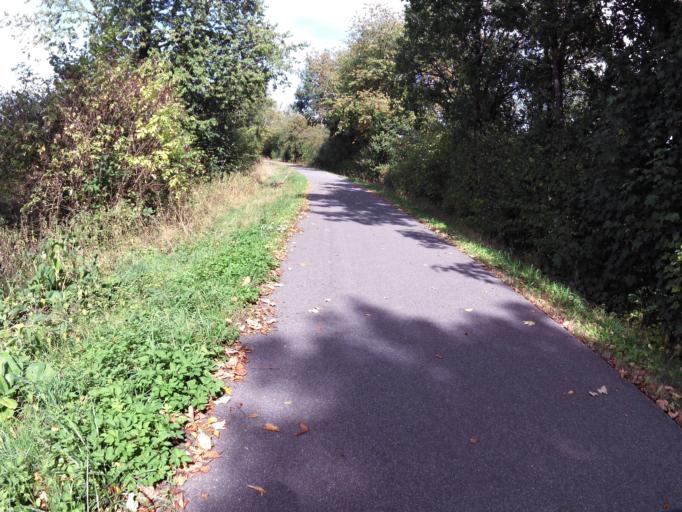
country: DE
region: Rheinland-Pfalz
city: Arzfeld
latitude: 50.0885
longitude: 6.2796
